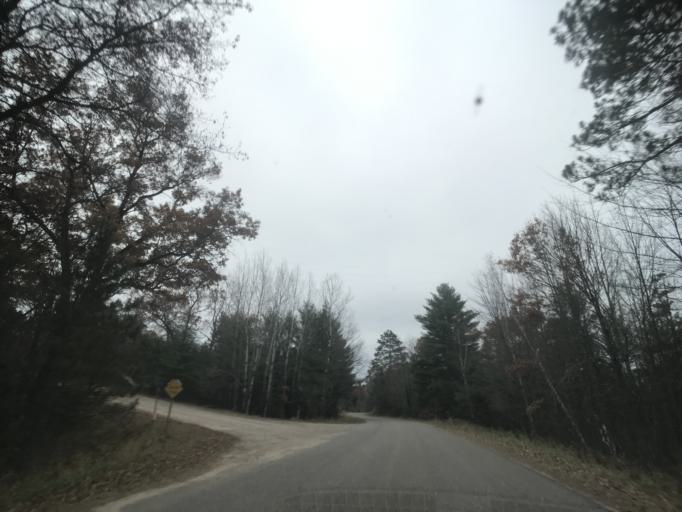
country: US
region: Wisconsin
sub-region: Oconto County
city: Gillett
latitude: 45.3761
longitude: -88.3213
